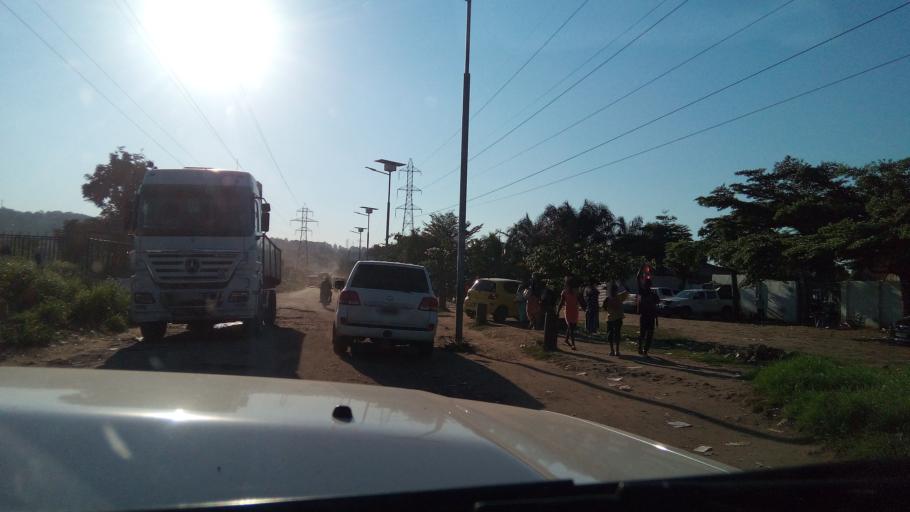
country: CD
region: Kinshasa
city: Kinshasa
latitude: -4.3577
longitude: 15.2682
